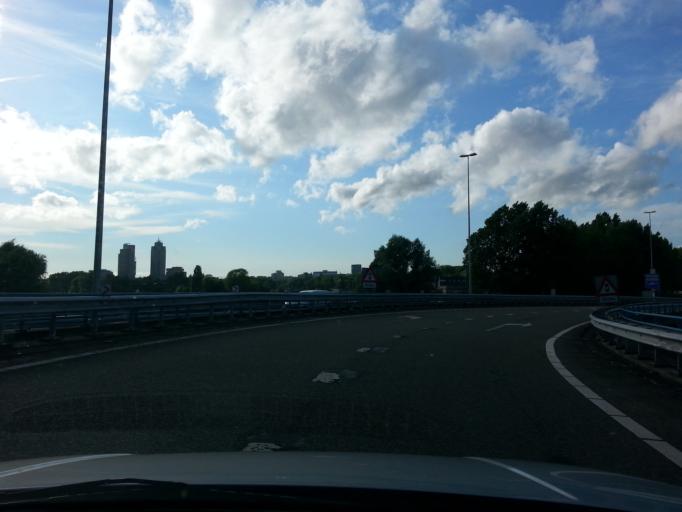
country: NL
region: North Holland
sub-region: Gemeente Ouder-Amstel
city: Duivendrecht
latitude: 52.3374
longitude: 4.9391
